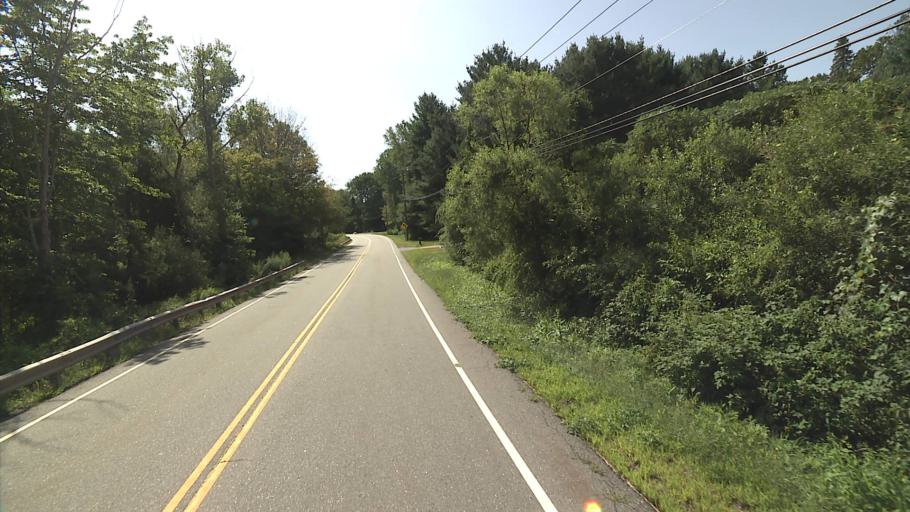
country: US
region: Connecticut
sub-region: New London County
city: Colchester
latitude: 41.6192
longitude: -72.2744
